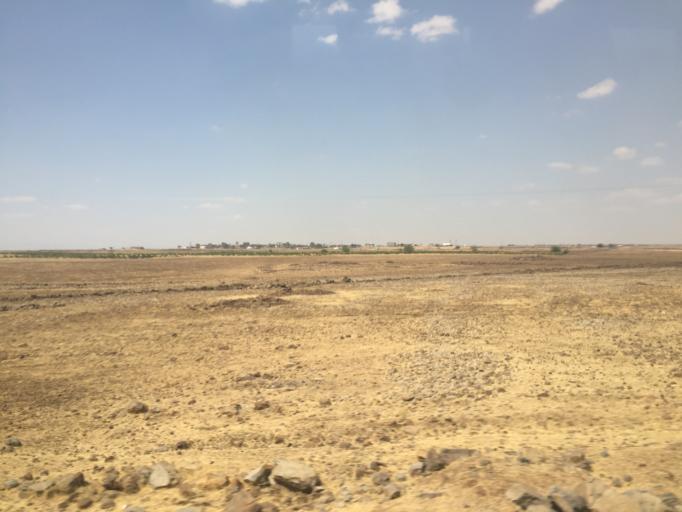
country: TR
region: Sanliurfa
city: Siverek
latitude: 37.7740
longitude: 39.4507
